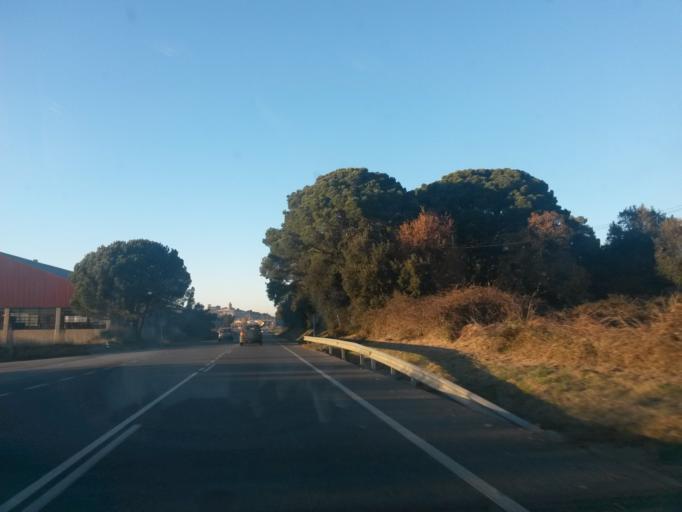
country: ES
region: Catalonia
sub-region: Provincia de Girona
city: Pals
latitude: 41.9618
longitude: 3.1528
